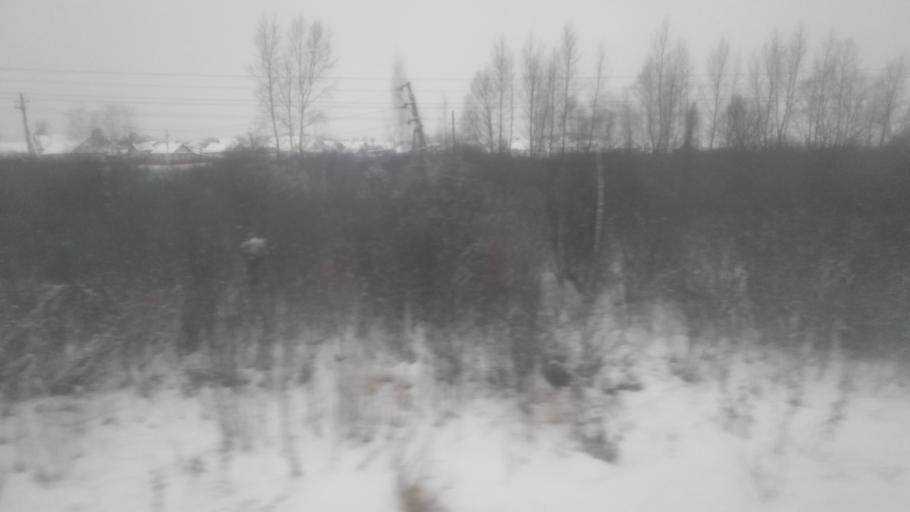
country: RU
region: Bashkortostan
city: Yanaul
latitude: 56.2805
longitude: 54.9574
